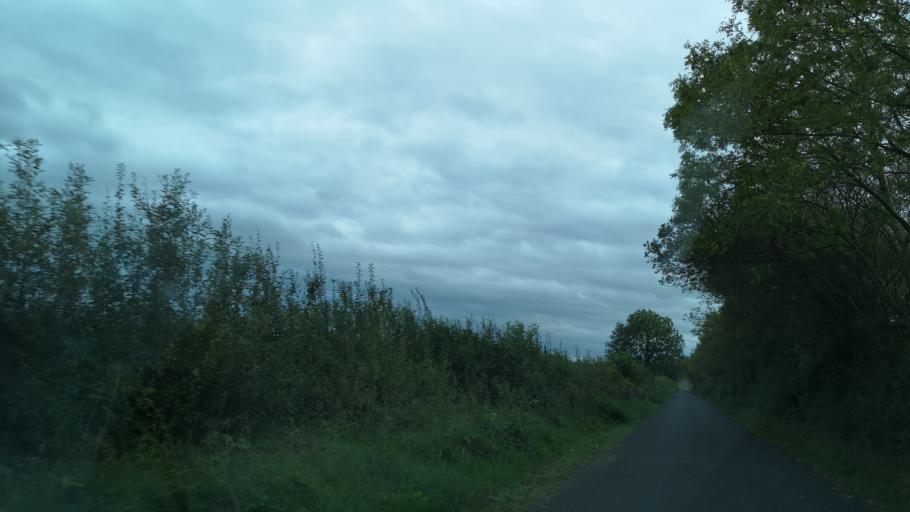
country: IE
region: Leinster
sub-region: Uibh Fhaili
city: Ferbane
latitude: 53.1904
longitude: -7.7264
